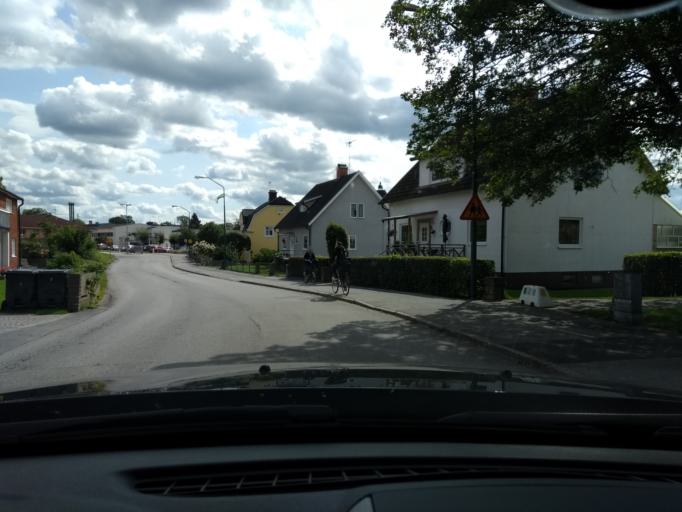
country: SE
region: Kalmar
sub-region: Vimmerby Kommun
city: Vimmerby
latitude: 57.6701
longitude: 15.8573
